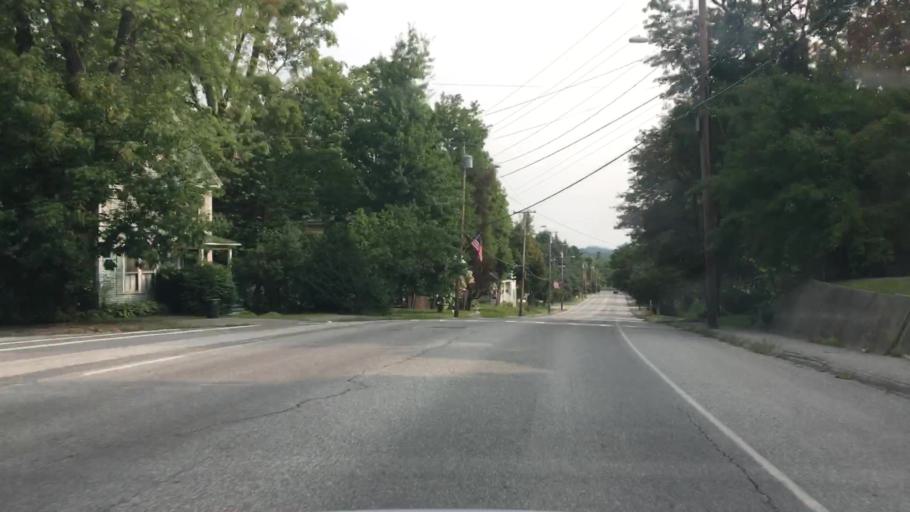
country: US
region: Maine
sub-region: Kennebec County
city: Gardiner
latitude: 44.2221
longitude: -69.7788
